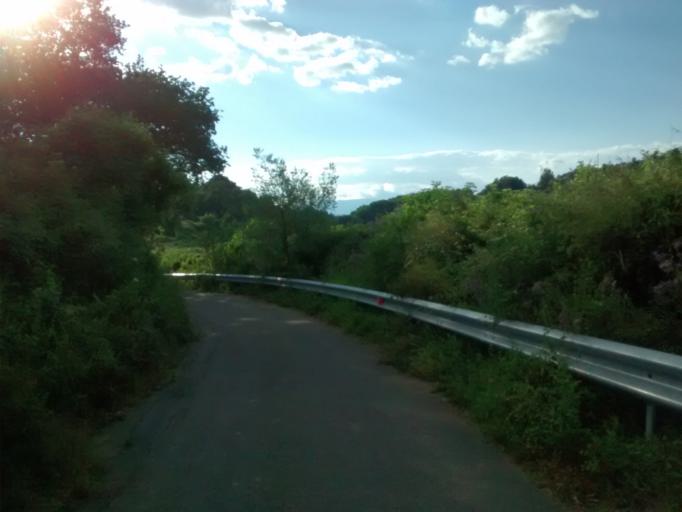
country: IT
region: Calabria
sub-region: Provincia di Catanzaro
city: Cortale
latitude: 38.8827
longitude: 16.4110
